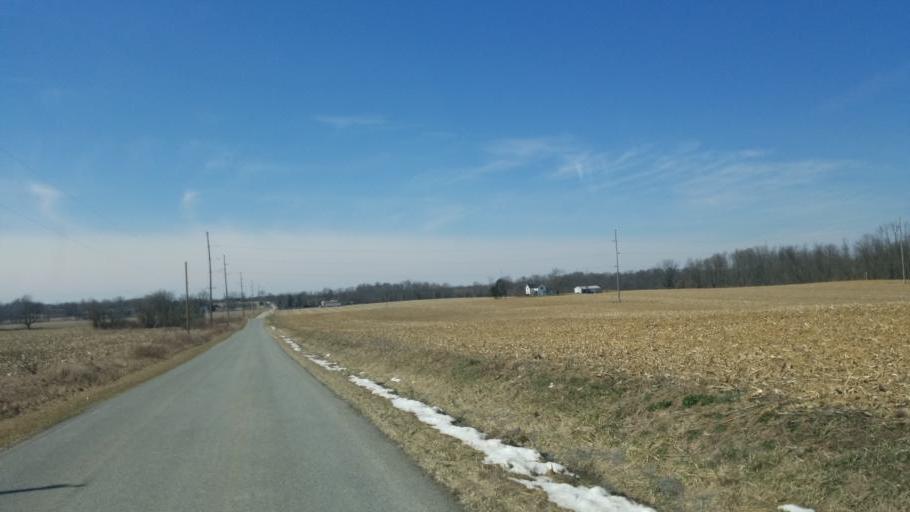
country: US
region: Ohio
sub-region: Crawford County
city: Galion
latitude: 40.6687
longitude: -82.7983
